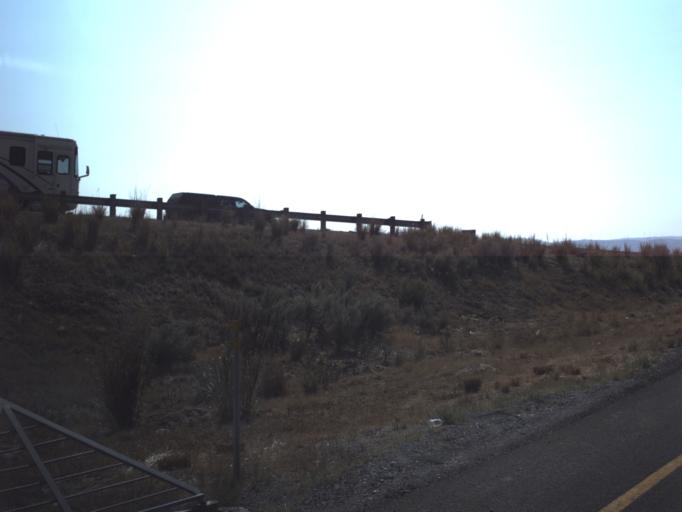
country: US
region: Wyoming
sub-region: Uinta County
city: Evanston
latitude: 41.1533
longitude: -111.1452
